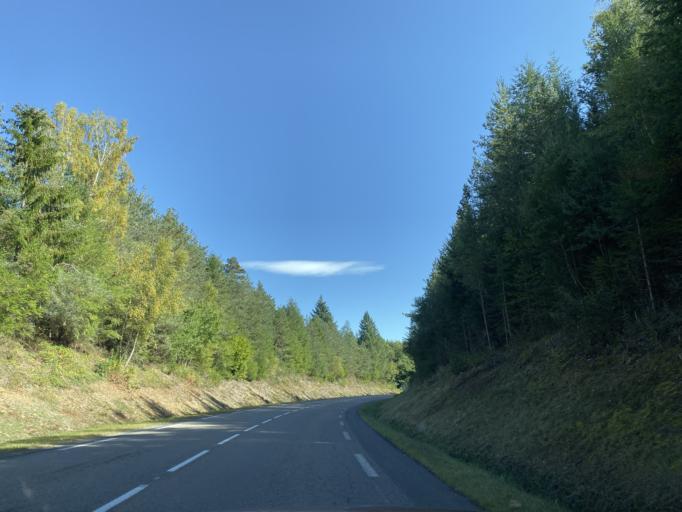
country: FR
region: Rhone-Alpes
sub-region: Departement de la Loire
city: Noiretable
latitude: 45.8417
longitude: 3.7897
